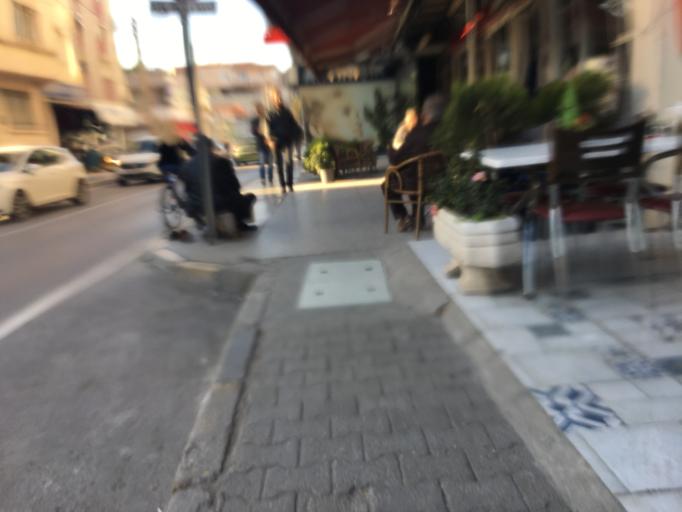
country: TR
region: Izmir
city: Buca
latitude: 38.3840
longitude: 27.1684
